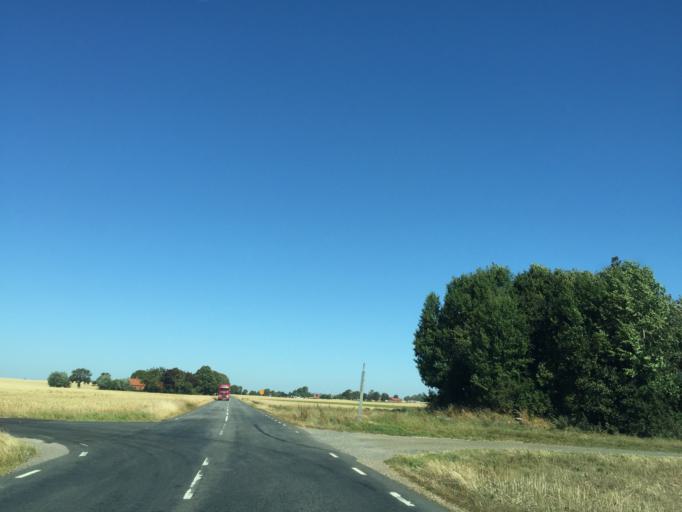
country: SE
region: Skane
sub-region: Ystads Kommun
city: Kopingebro
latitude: 55.4498
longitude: 14.1190
